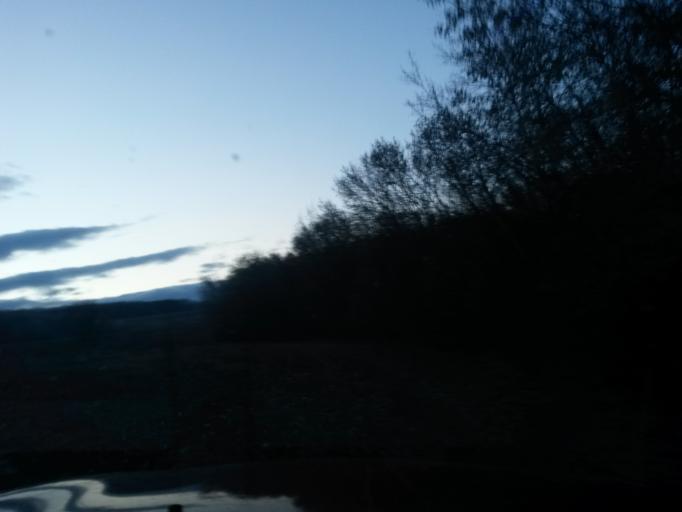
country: SK
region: Kosicky
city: Kosice
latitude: 48.7021
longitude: 21.3146
